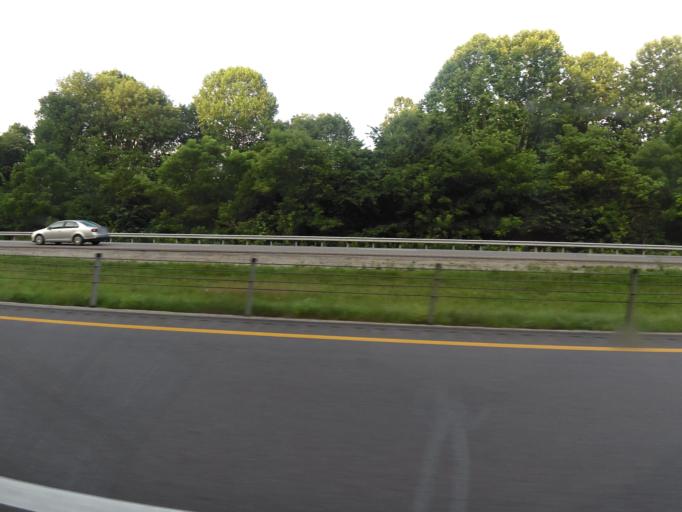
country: US
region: Kentucky
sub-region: Rockcastle County
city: Mount Vernon
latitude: 37.3891
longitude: -84.3362
